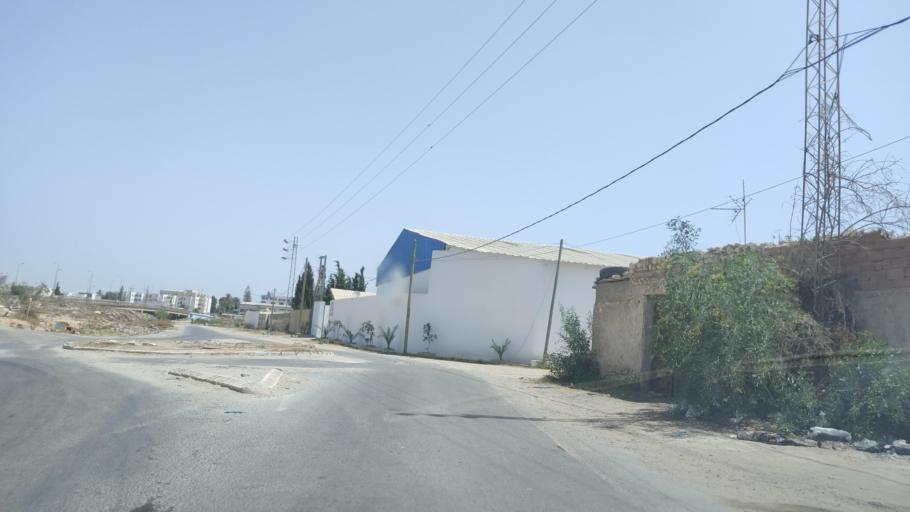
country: TN
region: Safaqis
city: Sfax
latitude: 34.7069
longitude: 10.7226
